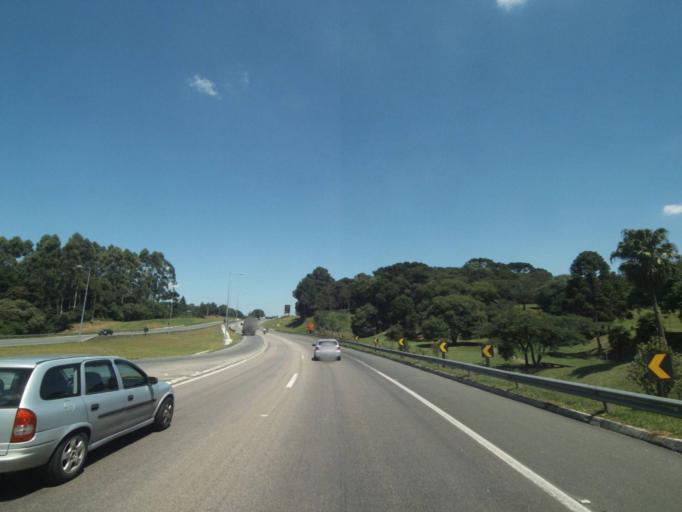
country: BR
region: Parana
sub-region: Araucaria
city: Araucaria
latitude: -25.5753
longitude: -49.3123
